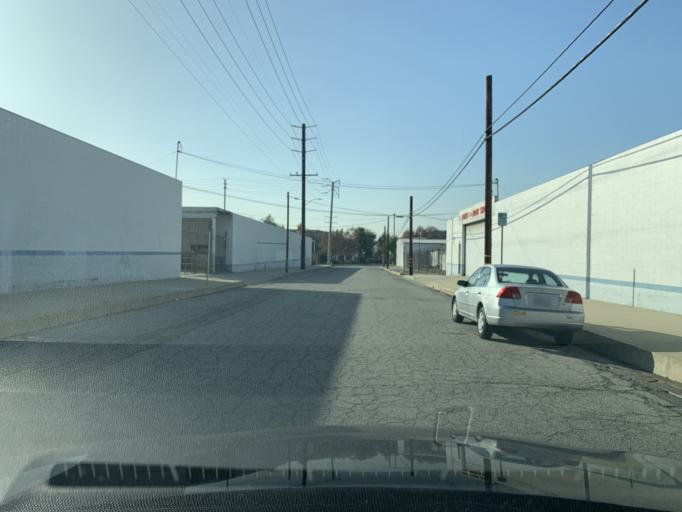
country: US
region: California
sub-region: Los Angeles County
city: Covina
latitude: 34.0910
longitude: -117.8909
